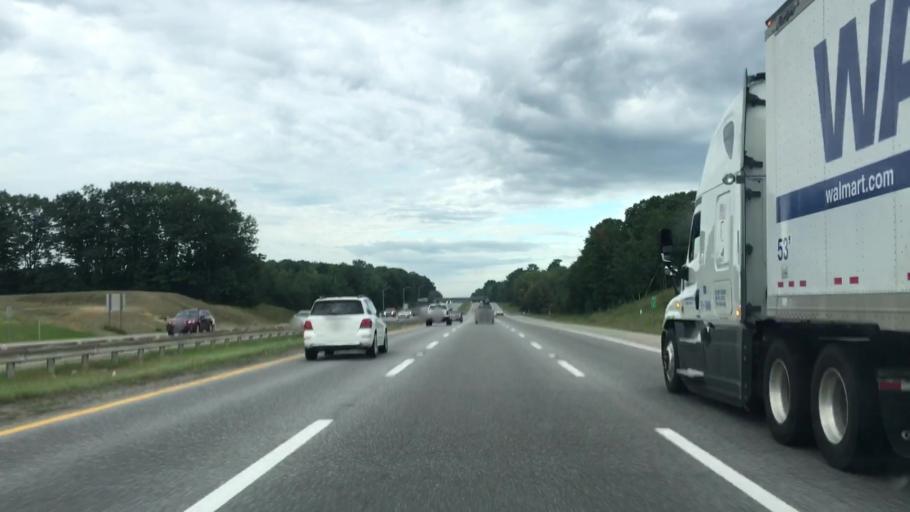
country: US
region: Maine
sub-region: York County
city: Saco
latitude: 43.5212
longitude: -70.4614
